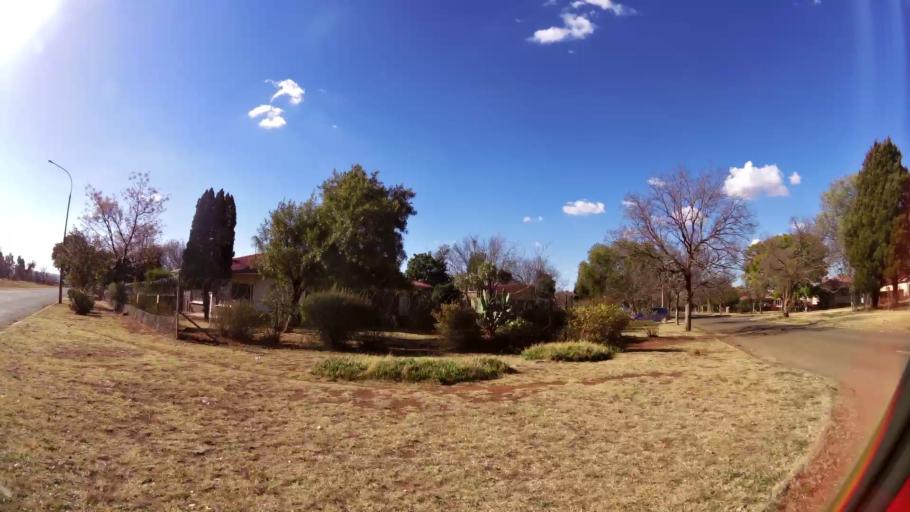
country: ZA
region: Gauteng
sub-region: West Rand District Municipality
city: Carletonville
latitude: -26.3642
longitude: 27.3614
